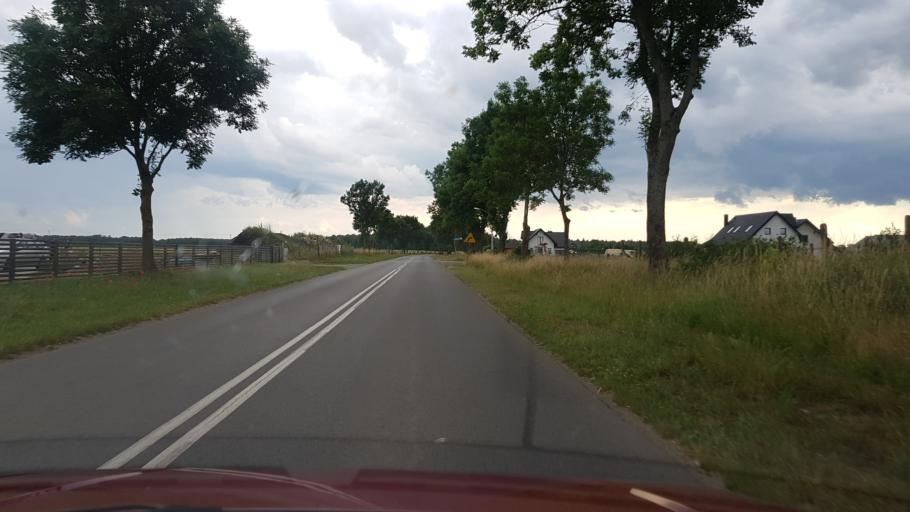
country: PL
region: West Pomeranian Voivodeship
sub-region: Powiat gryficki
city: Gryfice
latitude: 53.8928
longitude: 15.1735
